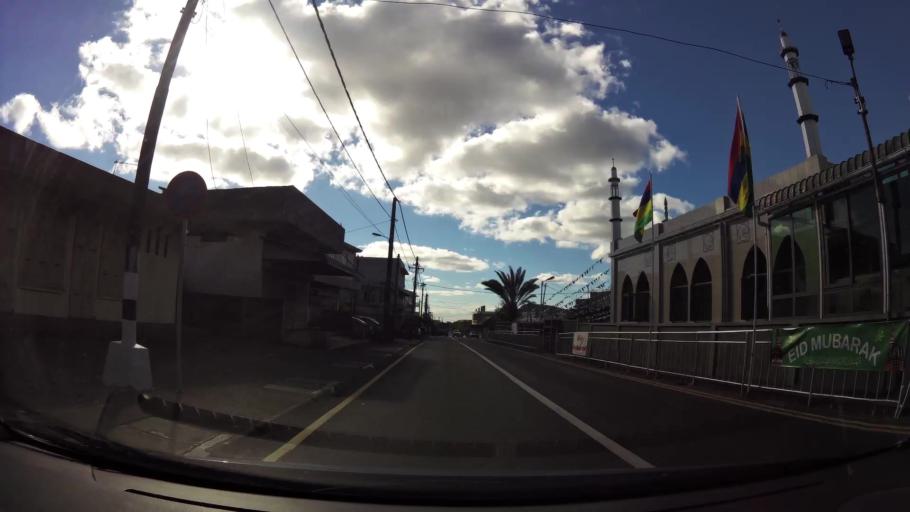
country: MU
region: Plaines Wilhems
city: Vacoas
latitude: -20.2972
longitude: 57.4839
